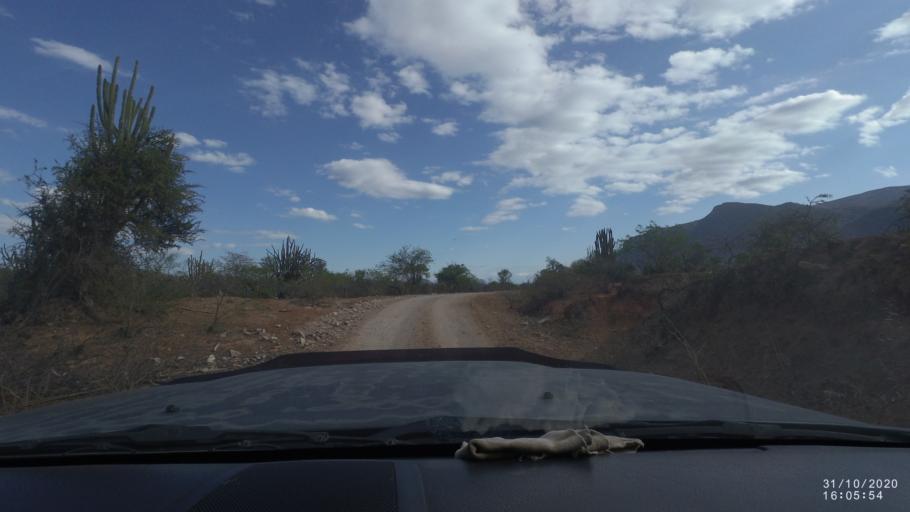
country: BO
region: Chuquisaca
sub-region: Provincia Zudanez
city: Mojocoya
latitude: -18.3699
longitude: -64.6486
